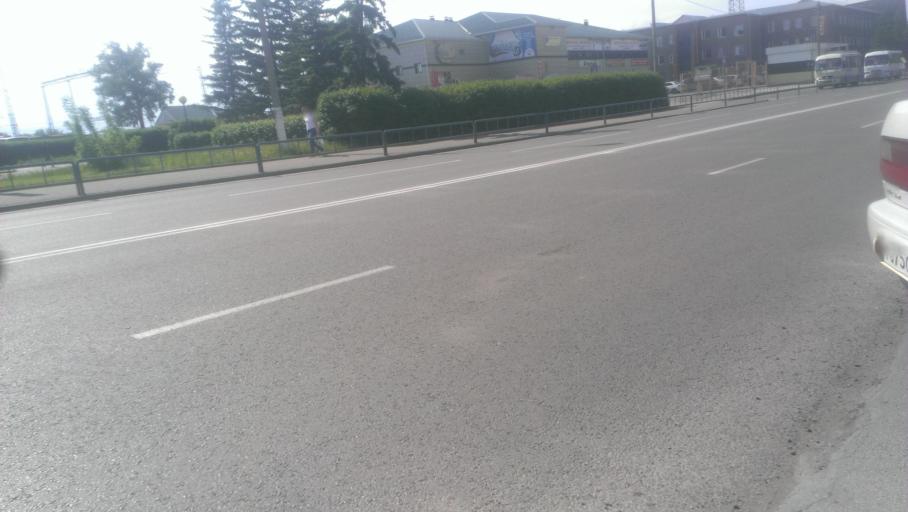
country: RU
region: Altai Krai
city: Novoaltaysk
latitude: 53.3924
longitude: 83.9347
